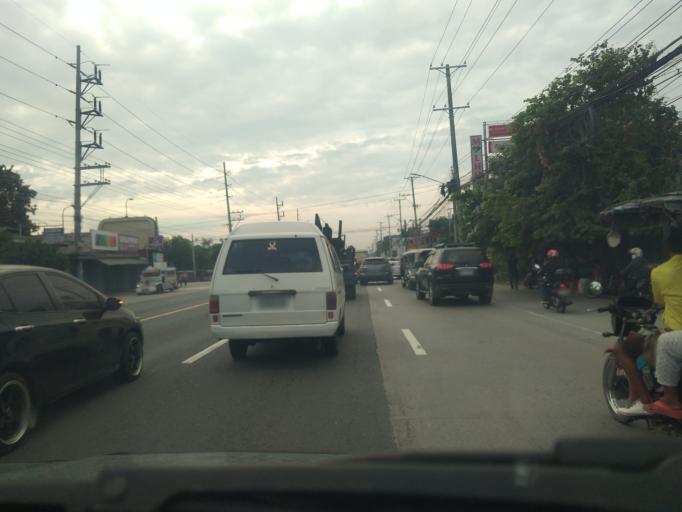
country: PH
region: Central Luzon
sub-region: Province of Pampanga
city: Bulaon
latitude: 15.0598
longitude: 120.6562
